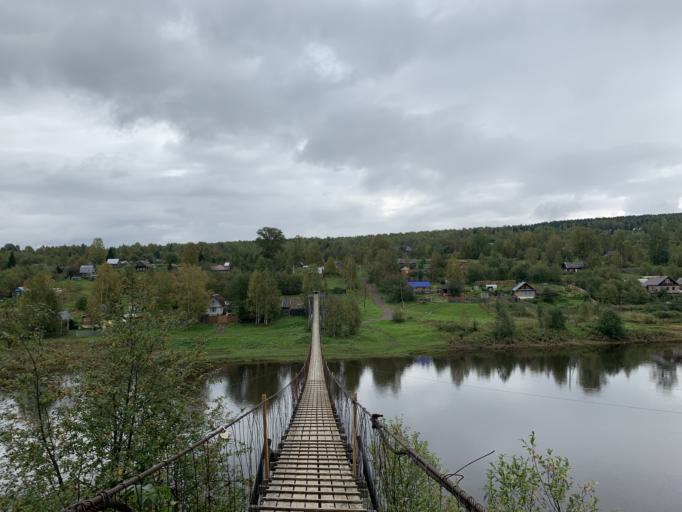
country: RU
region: Perm
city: Gubakha
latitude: 58.8636
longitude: 57.6103
